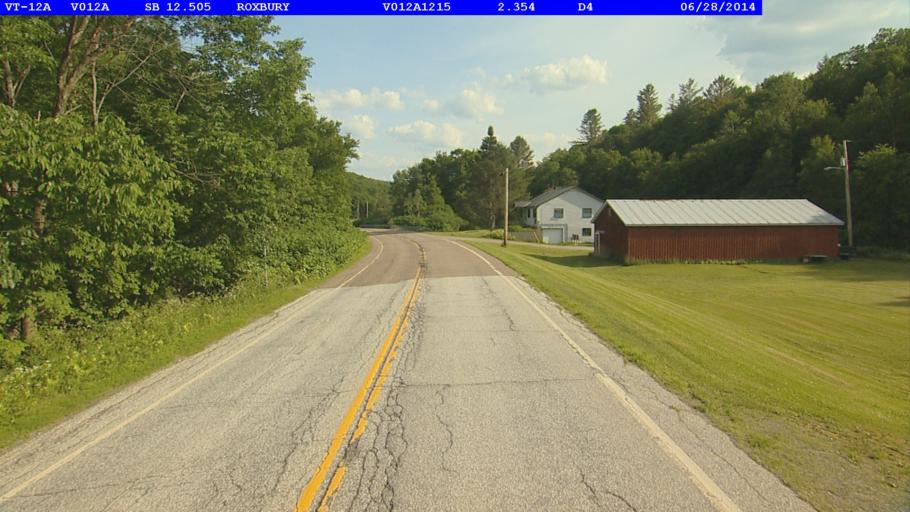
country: US
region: Vermont
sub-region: Washington County
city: Northfield
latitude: 44.0624
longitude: -72.7433
